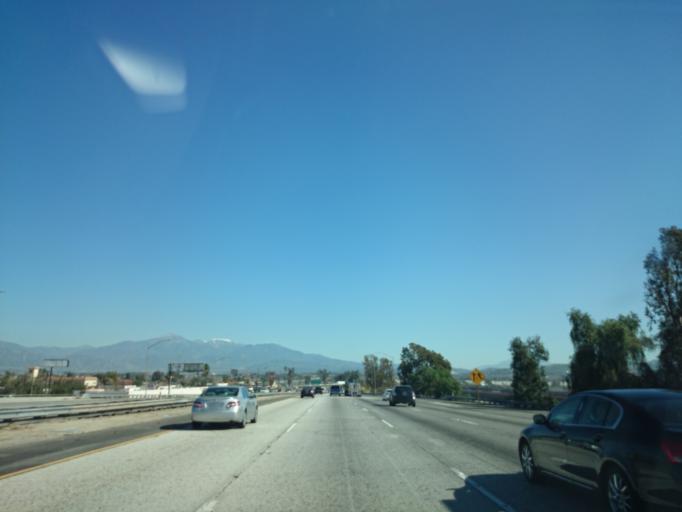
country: US
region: California
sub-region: San Bernardino County
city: Colton
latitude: 34.0655
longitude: -117.3214
